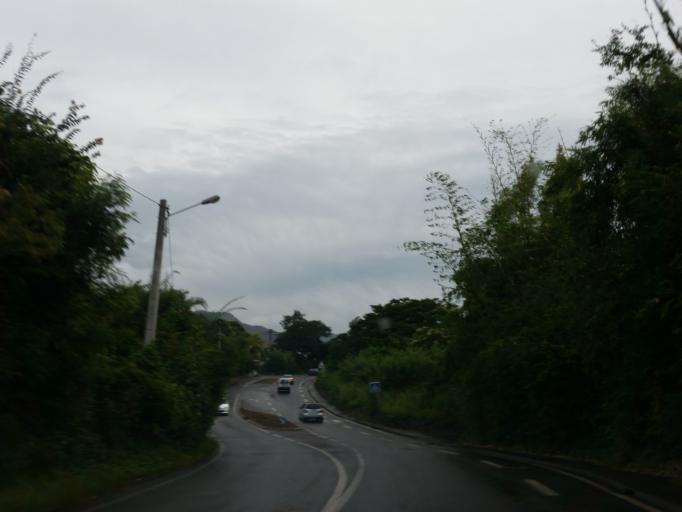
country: RE
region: Reunion
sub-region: Reunion
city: Sainte-Marie
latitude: -20.9096
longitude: 55.5023
